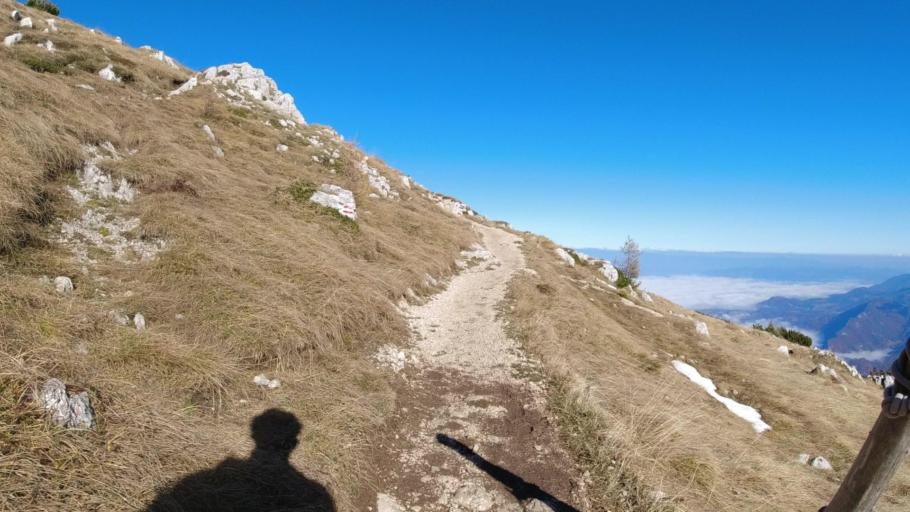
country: AT
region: Carinthia
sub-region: Politischer Bezirk Volkermarkt
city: Gallizien
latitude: 46.5049
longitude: 14.4869
